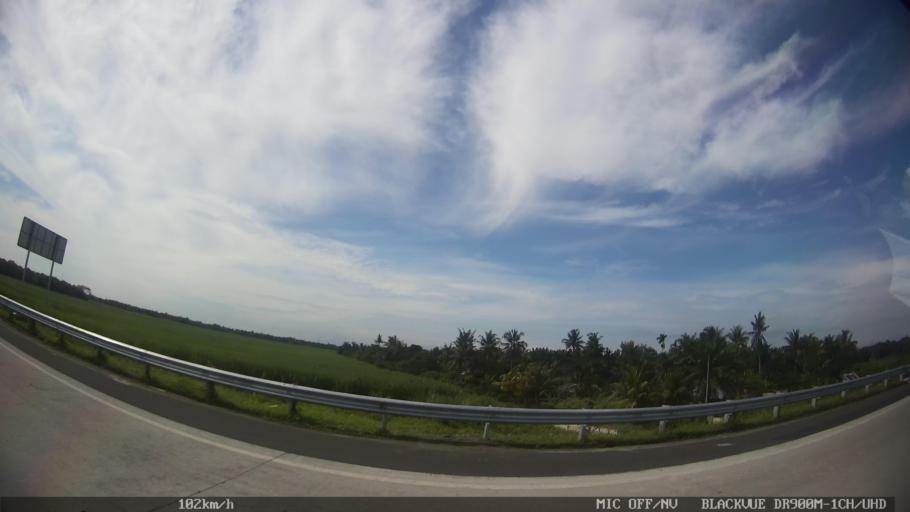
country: ID
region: North Sumatra
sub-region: Kabupaten Langkat
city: Stabat
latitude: 3.7132
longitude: 98.5129
